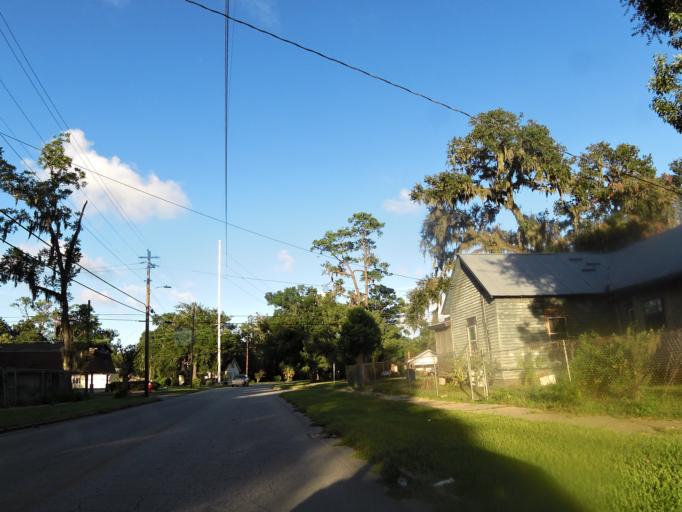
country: US
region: Georgia
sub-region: Glynn County
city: Brunswick
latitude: 31.1548
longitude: -81.4850
